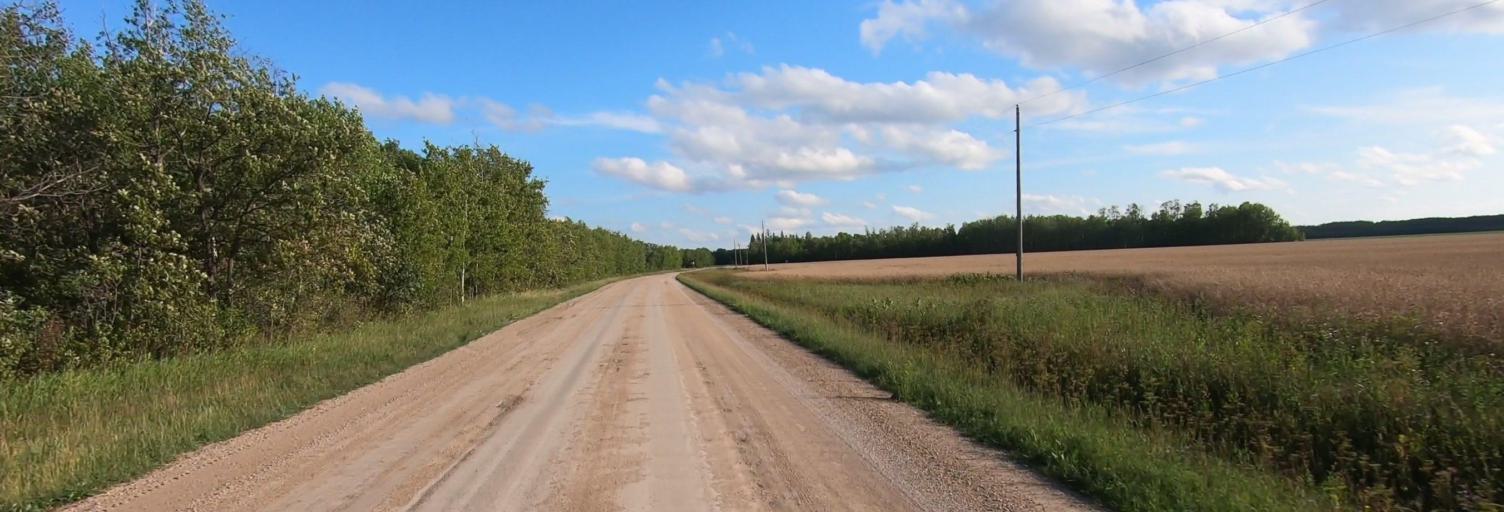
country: CA
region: Manitoba
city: Selkirk
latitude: 50.2282
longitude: -96.8396
